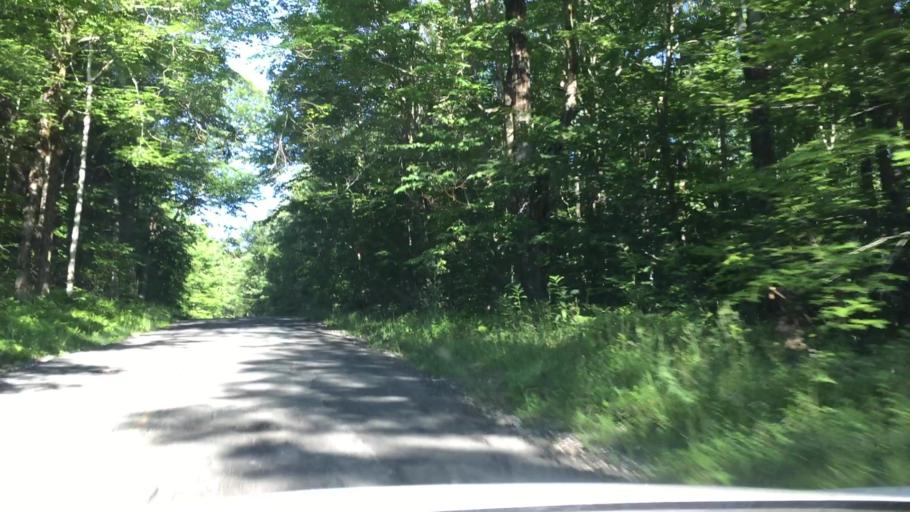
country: US
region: Massachusetts
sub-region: Berkshire County
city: Becket
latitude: 42.2998
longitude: -73.1376
